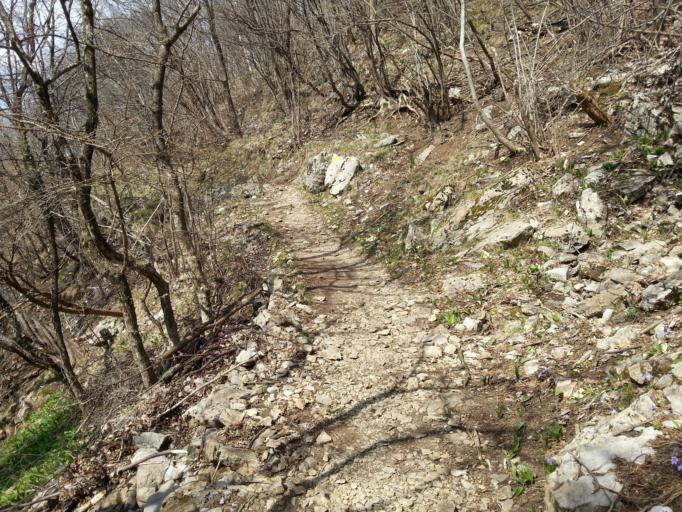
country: IT
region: Lombardy
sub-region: Provincia di Lecco
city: Suello
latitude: 45.8443
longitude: 9.3157
